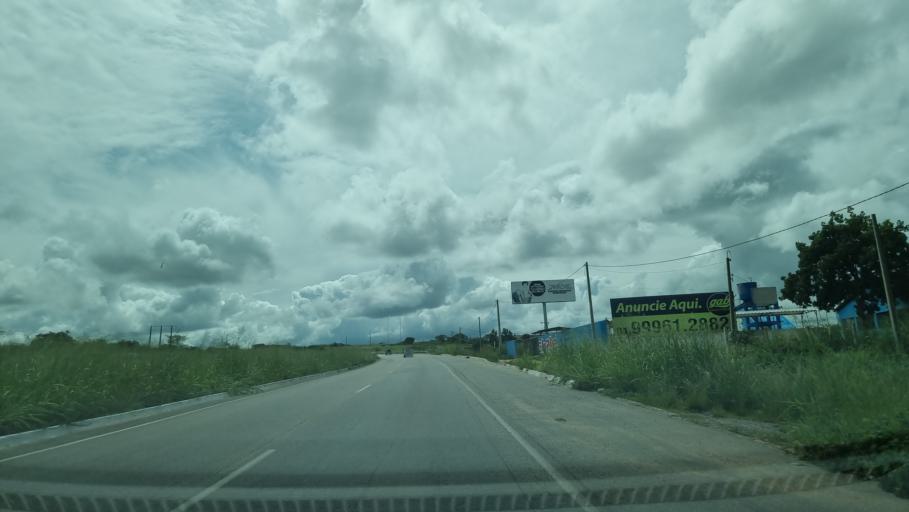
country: BR
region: Pernambuco
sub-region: Caruaru
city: Caruaru
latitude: -8.3313
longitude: -35.9820
